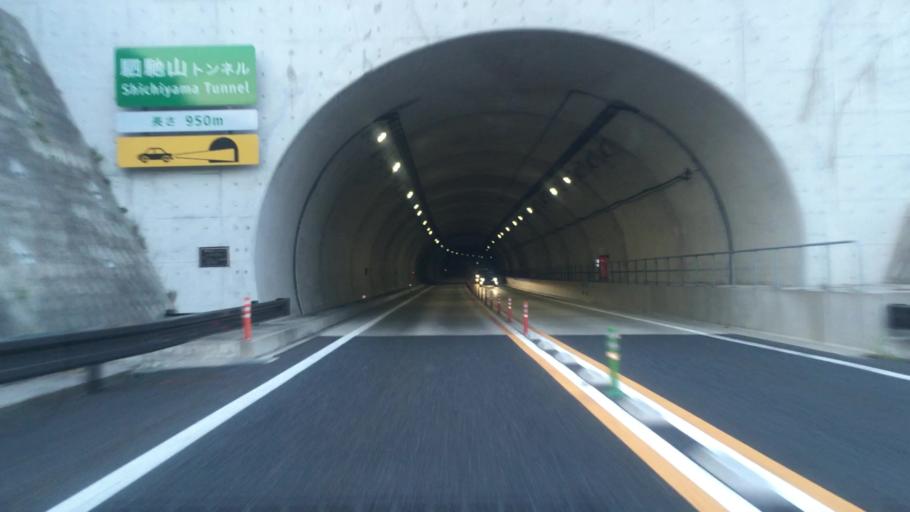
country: JP
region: Tottori
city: Tottori
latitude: 35.5610
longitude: 134.2847
